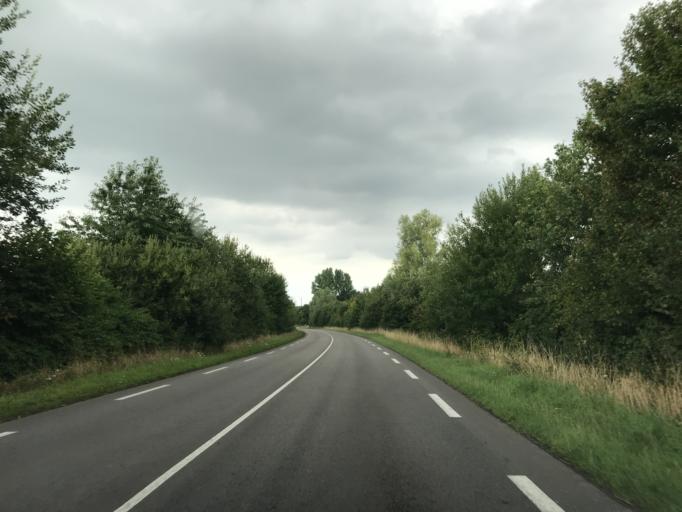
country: FR
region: Haute-Normandie
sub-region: Departement de la Seine-Maritime
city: Bolbec
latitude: 49.5772
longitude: 0.4545
